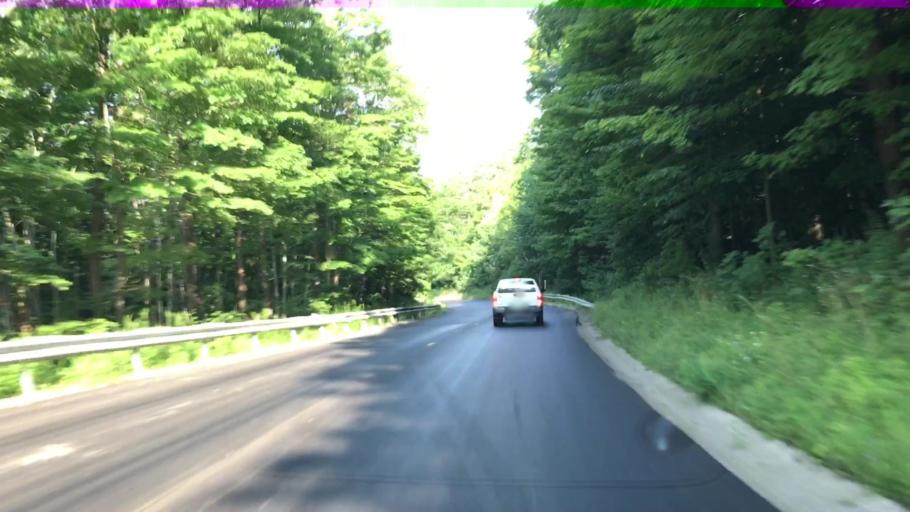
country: US
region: New York
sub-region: Chautauqua County
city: Brocton
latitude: 42.3184
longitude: -79.3497
